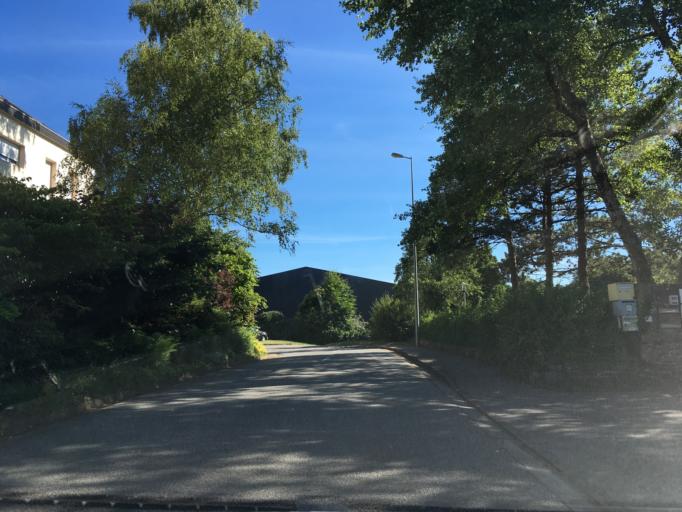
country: FR
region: Brittany
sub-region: Departement du Finistere
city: Quimper
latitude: 47.9871
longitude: -4.0853
